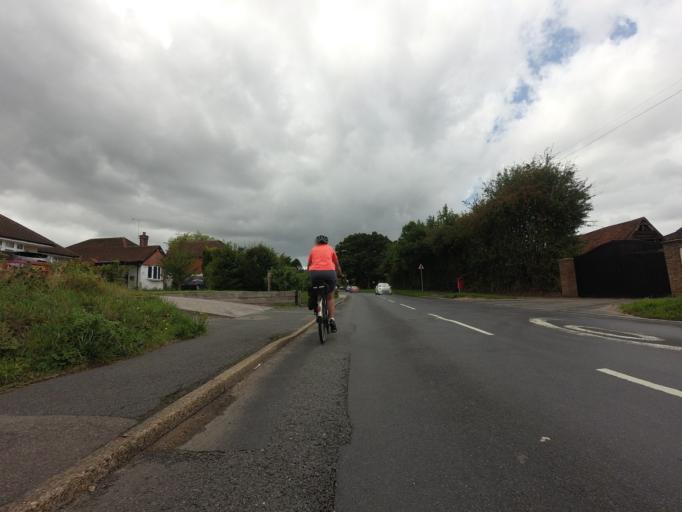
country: GB
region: England
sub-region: Kent
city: Shoreham
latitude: 51.3115
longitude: 0.1776
